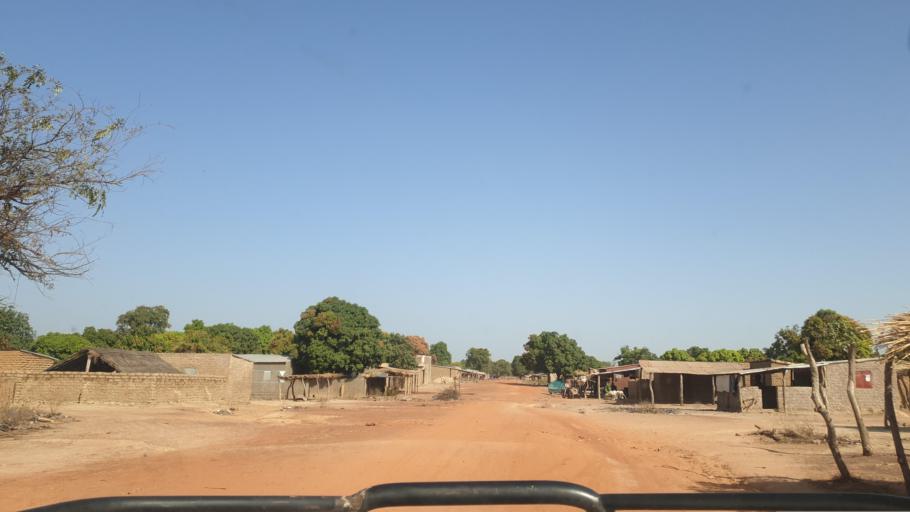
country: ML
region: Sikasso
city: Kolondieba
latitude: 11.7660
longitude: -6.9021
